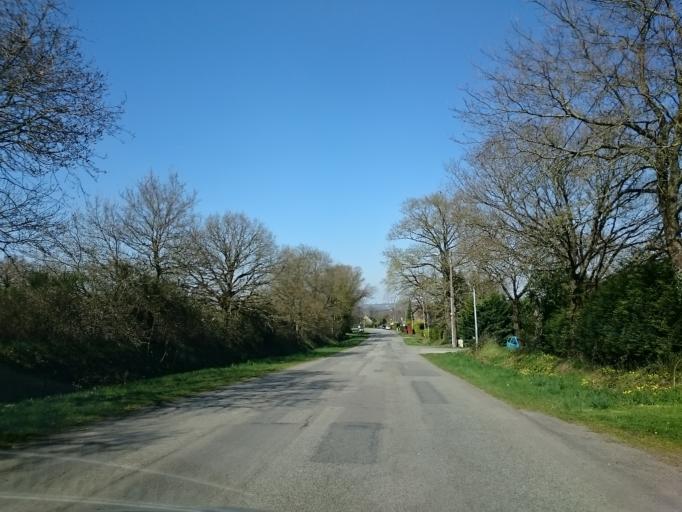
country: FR
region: Brittany
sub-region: Departement d'Ille-et-Vilaine
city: Laille
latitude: 47.9789
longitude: -1.6932
